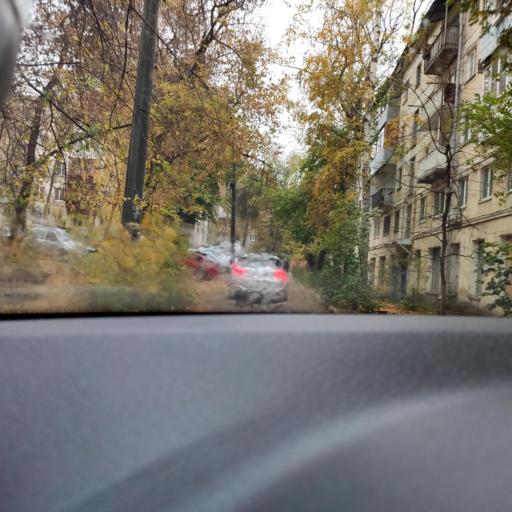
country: RU
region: Samara
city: Samara
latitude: 53.2101
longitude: 50.1653
